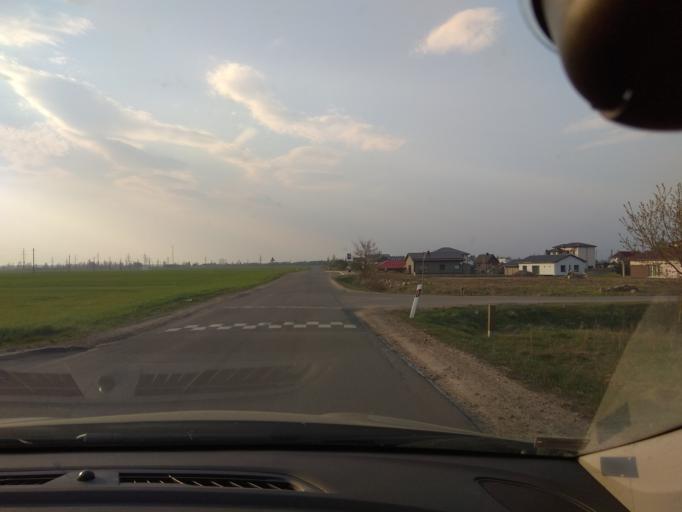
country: LT
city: Baltoji Voke
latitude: 54.6033
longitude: 25.1348
